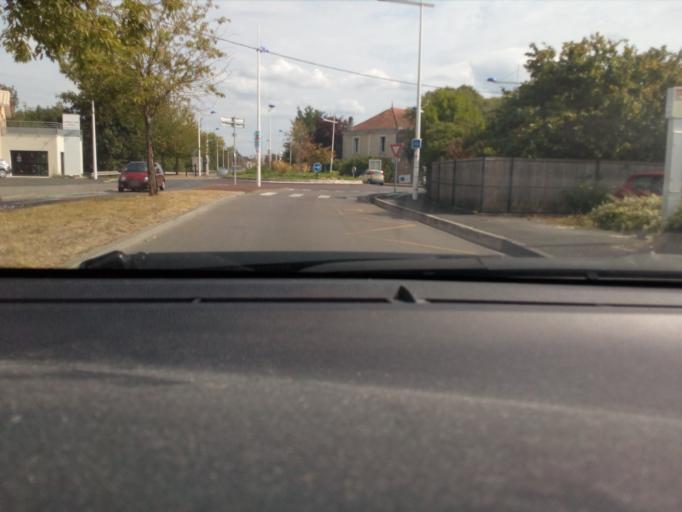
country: FR
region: Poitou-Charentes
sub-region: Departement de la Charente
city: Angouleme
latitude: 45.6628
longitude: 0.1556
